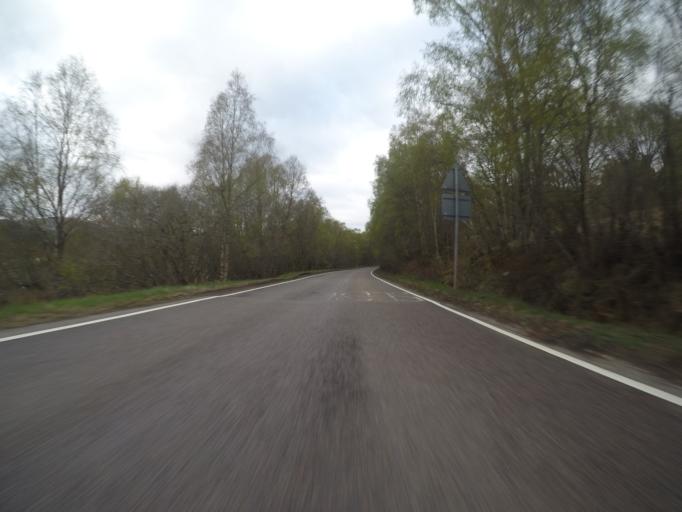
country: GB
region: Scotland
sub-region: Highland
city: Kingussie
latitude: 56.9714
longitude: -4.4305
